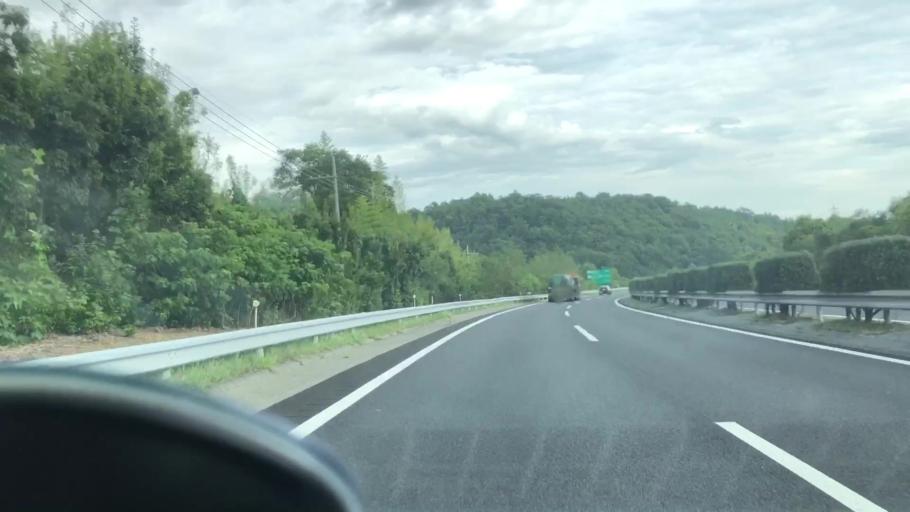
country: JP
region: Hyogo
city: Yashiro
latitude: 34.9397
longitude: 134.8766
